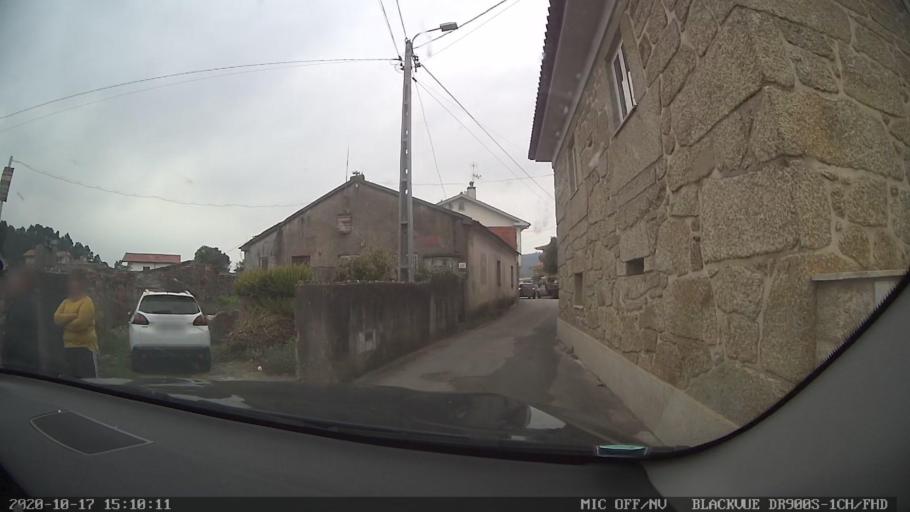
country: PT
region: Braga
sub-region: Esposende
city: Esposende
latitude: 41.5328
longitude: -8.7385
